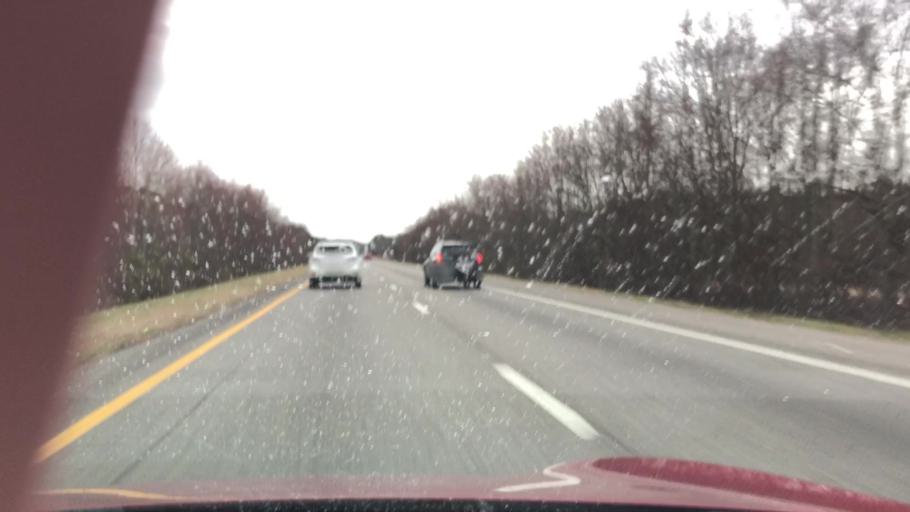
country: US
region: South Carolina
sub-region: Dillon County
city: Latta
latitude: 34.3279
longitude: -79.5704
